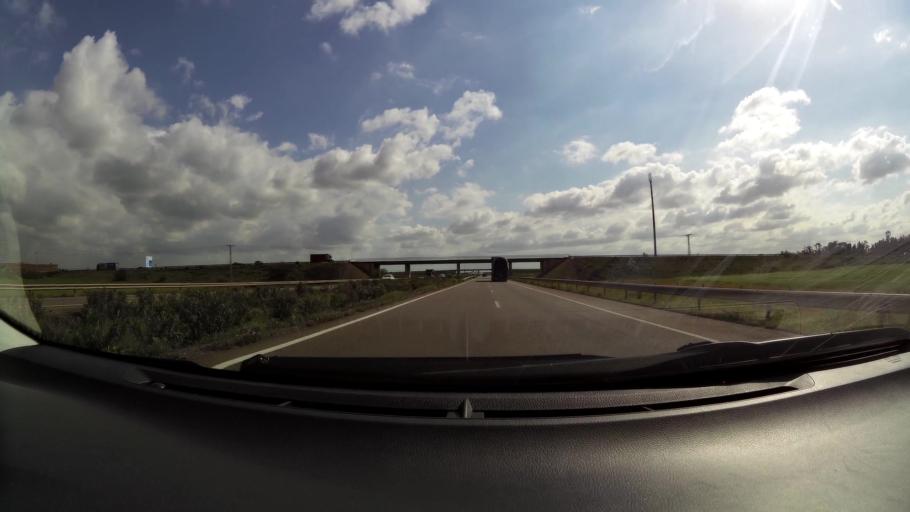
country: MA
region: Chaouia-Ouardigha
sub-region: Settat Province
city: Berrechid
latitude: 33.2507
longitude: -7.5623
